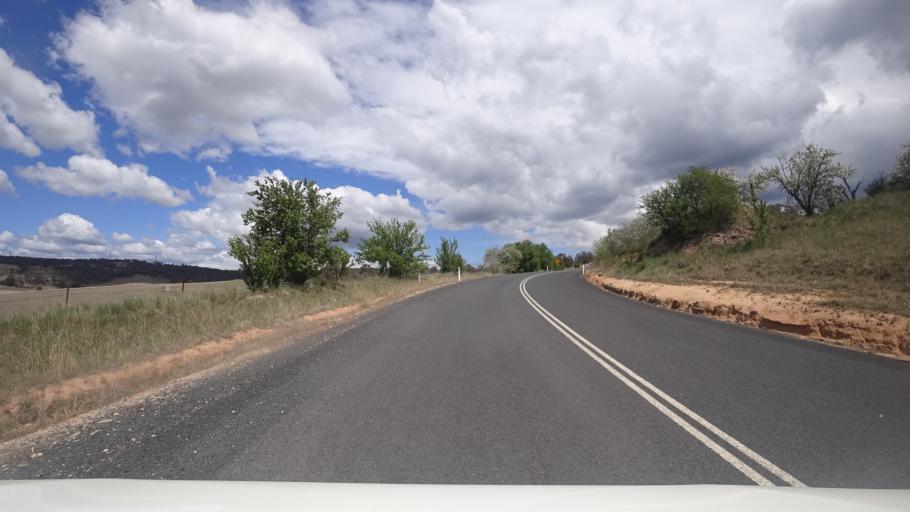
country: AU
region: New South Wales
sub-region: Oberon
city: Oberon
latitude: -33.5851
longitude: 149.8934
